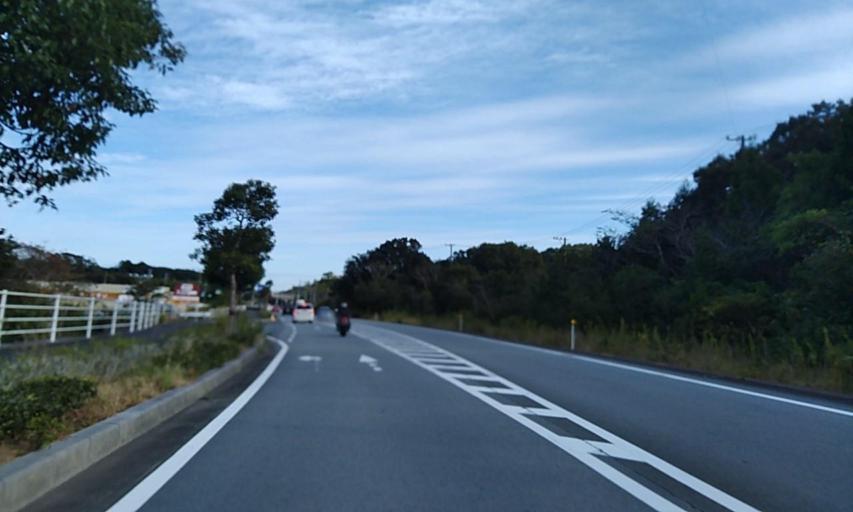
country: JP
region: Mie
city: Toba
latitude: 34.3524
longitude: 136.8092
